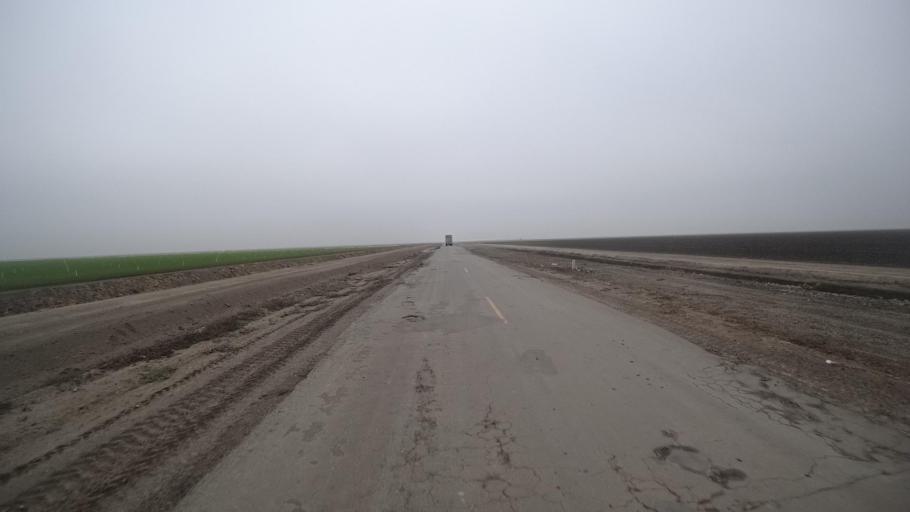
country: US
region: California
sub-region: Kern County
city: Rosedale
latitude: 35.1845
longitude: -119.1992
